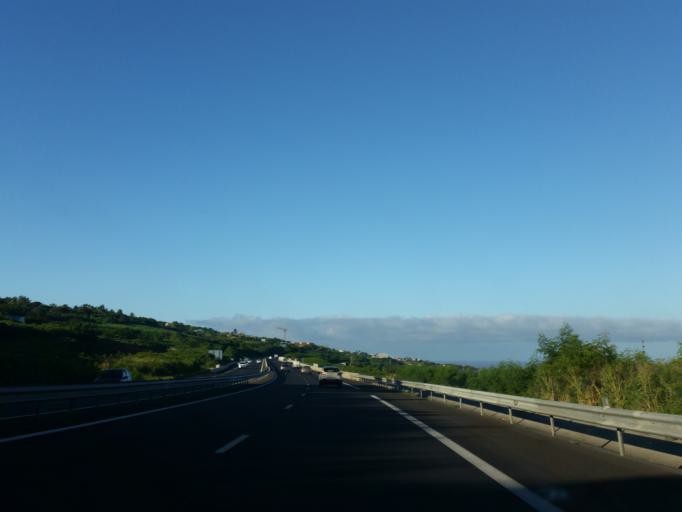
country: RE
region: Reunion
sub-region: Reunion
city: Saint-Leu
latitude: -21.1812
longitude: 55.2963
